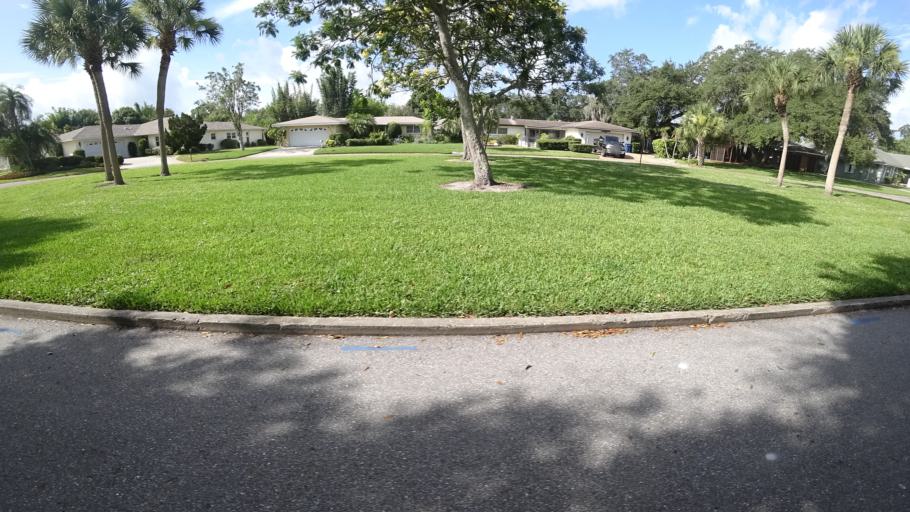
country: US
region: Florida
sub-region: Sarasota County
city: Desoto Lakes
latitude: 27.4036
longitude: -82.4968
